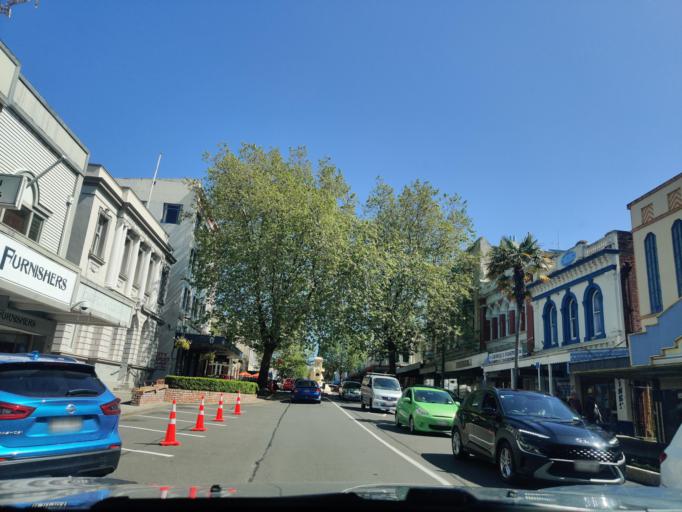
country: NZ
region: Manawatu-Wanganui
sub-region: Wanganui District
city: Wanganui
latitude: -39.9344
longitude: 175.0545
